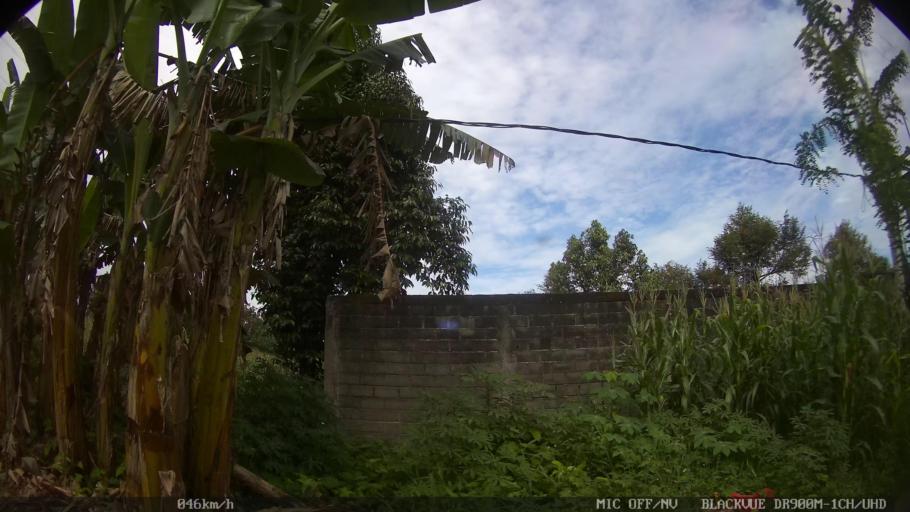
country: ID
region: North Sumatra
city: Sunggal
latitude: 3.5907
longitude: 98.5830
